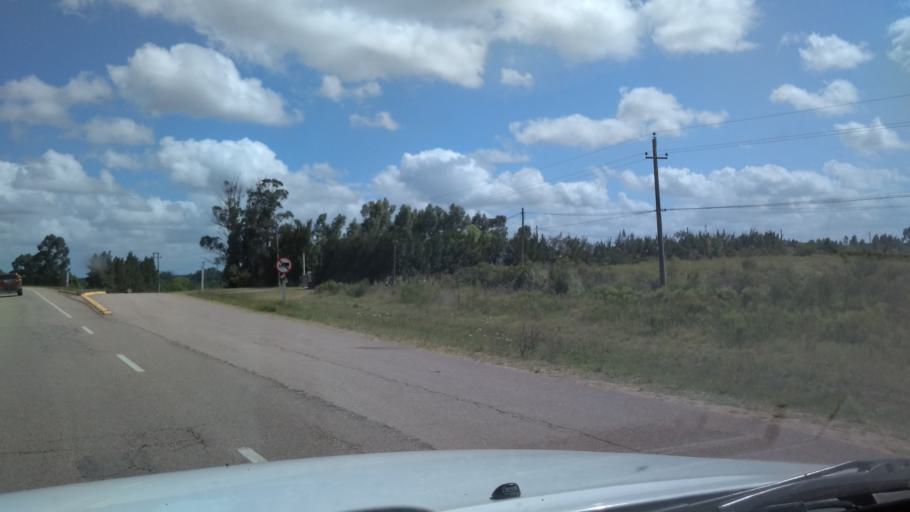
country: UY
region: Canelones
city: Sauce
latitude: -34.6373
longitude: -56.0526
